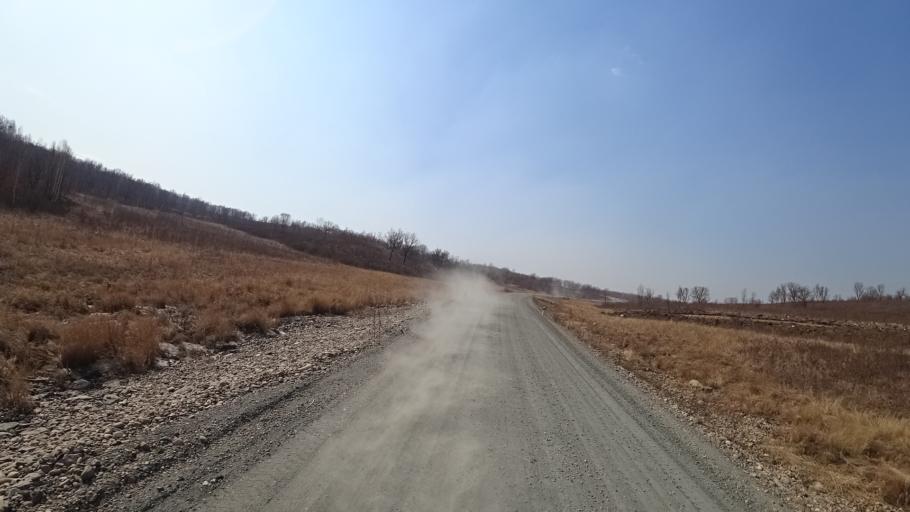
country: RU
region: Amur
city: Novobureyskiy
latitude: 49.8221
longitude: 129.9998
